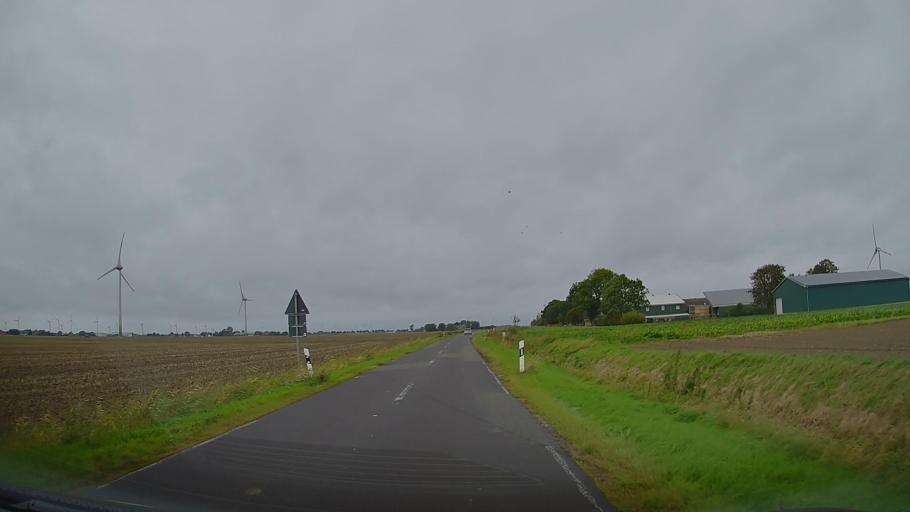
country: DE
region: Schleswig-Holstein
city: Marnerdeich
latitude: 53.9214
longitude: 8.9888
